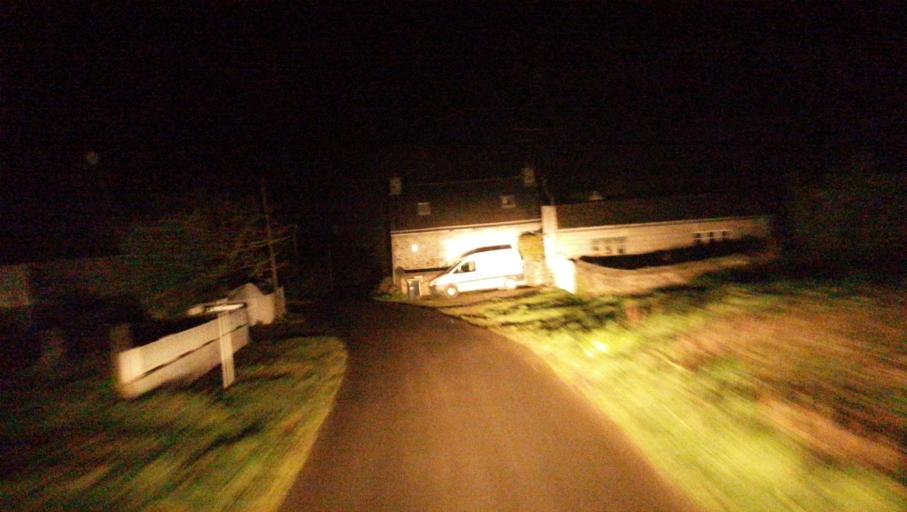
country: FR
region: Brittany
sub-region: Departement des Cotes-d'Armor
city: Lanvollon
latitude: 48.6469
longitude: -3.0145
